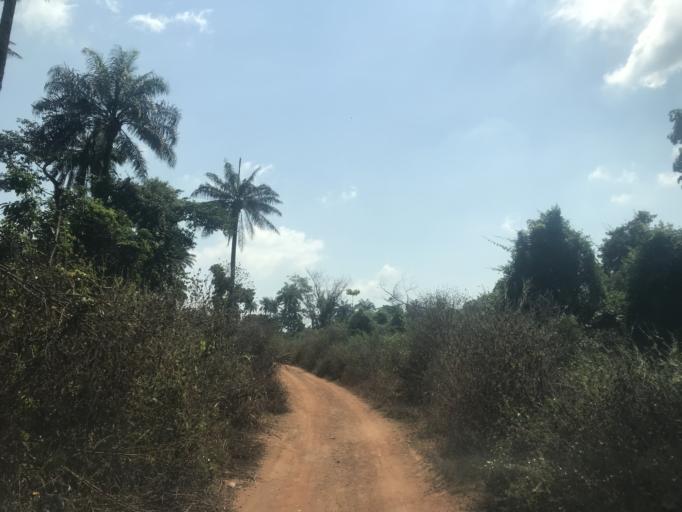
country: NG
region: Osun
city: Oke Mesi
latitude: 7.8892
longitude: 4.8828
